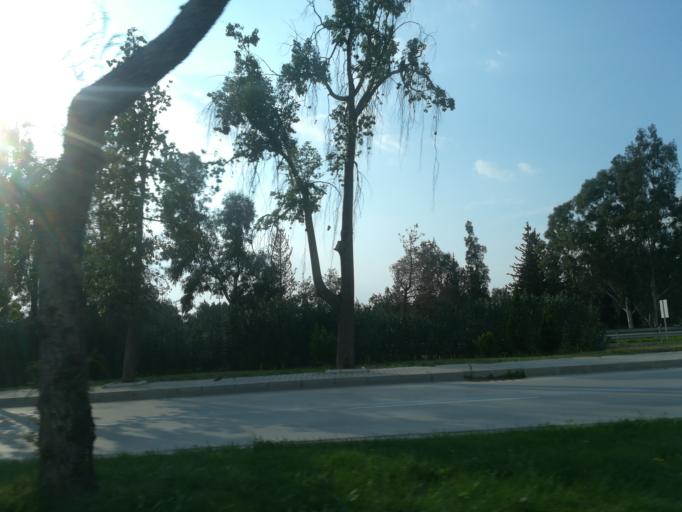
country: TR
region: Adana
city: Adana
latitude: 37.0262
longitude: 35.3442
